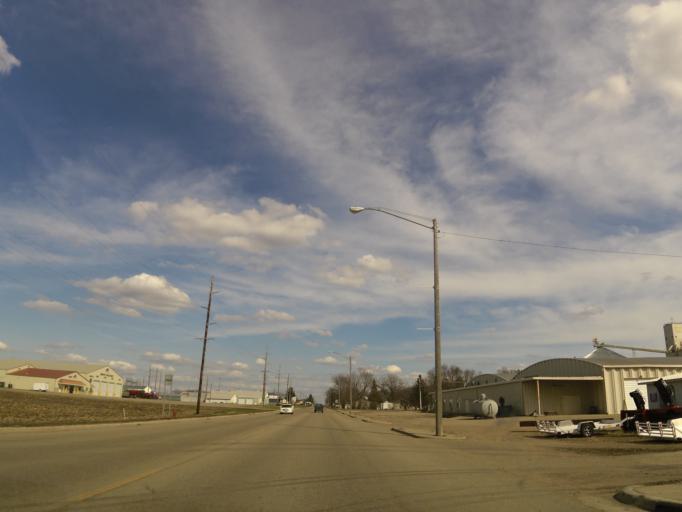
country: US
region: Minnesota
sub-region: Lac qui Parle County
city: Dawson
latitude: 44.9357
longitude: -96.0618
